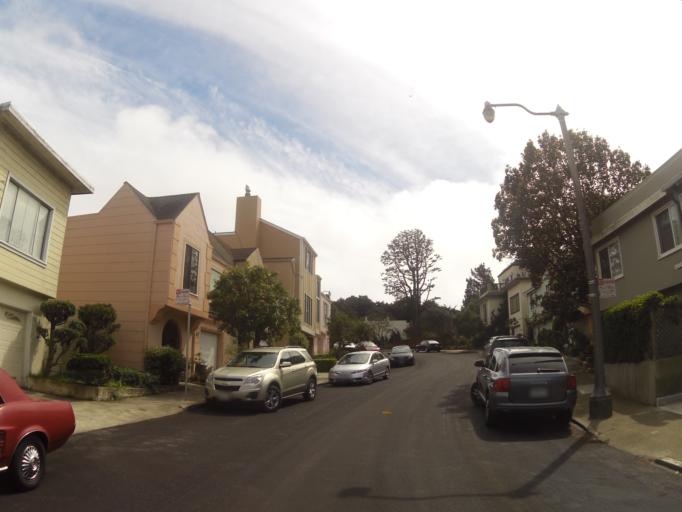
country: US
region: California
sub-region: San Mateo County
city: Daly City
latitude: 37.7521
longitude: -122.4696
